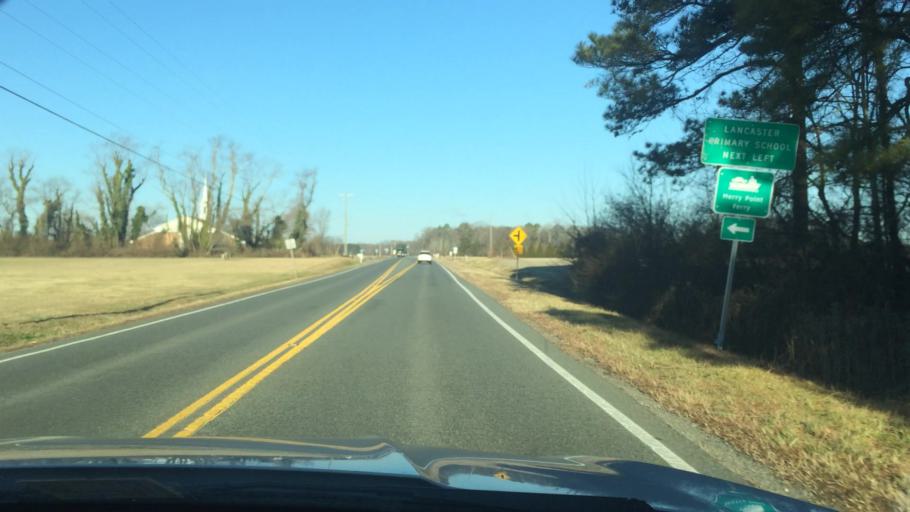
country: US
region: Virginia
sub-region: Lancaster County
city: Kilmarnock
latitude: 37.7517
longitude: -76.4101
